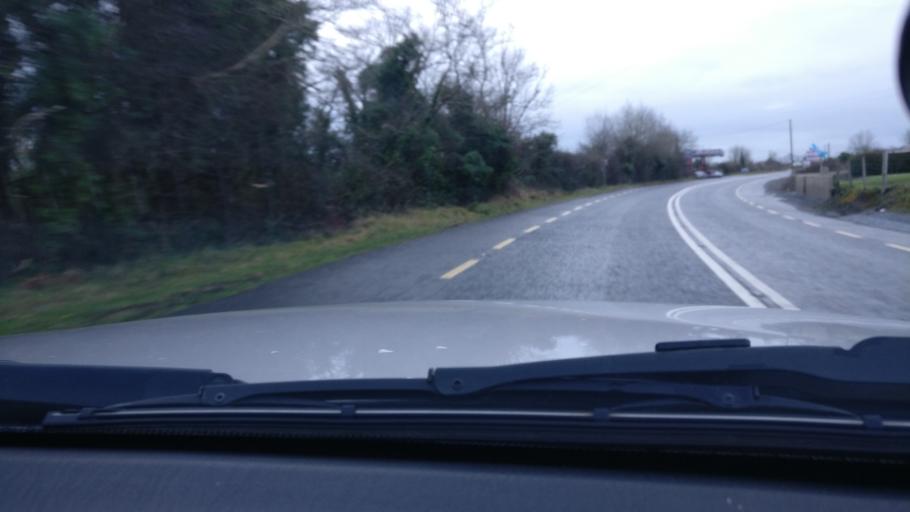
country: IE
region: Leinster
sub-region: An Iarmhi
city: Athlone
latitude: 53.3811
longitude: -7.9951
